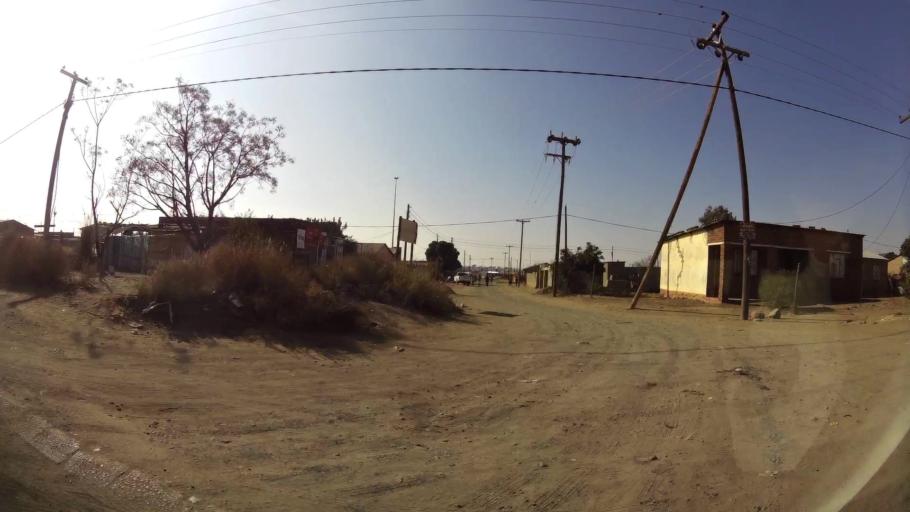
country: ZA
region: Orange Free State
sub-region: Mangaung Metropolitan Municipality
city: Bloemfontein
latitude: -29.1929
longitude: 26.2473
